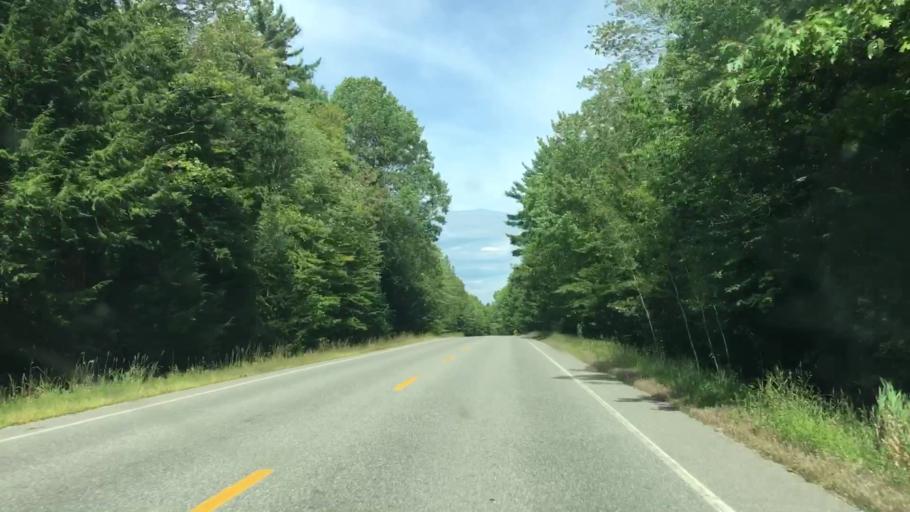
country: US
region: Maine
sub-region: Penobscot County
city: Lincoln
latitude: 45.3768
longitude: -68.5508
